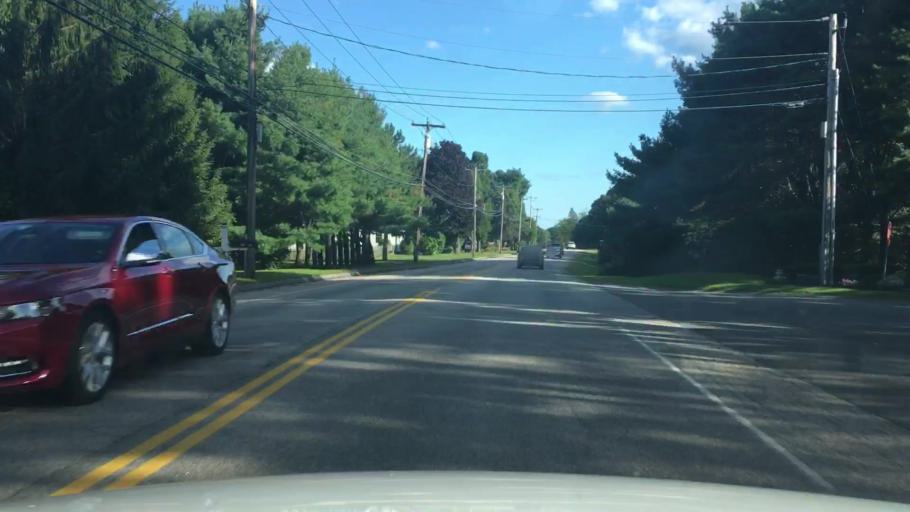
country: US
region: Maine
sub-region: Cumberland County
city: Scarborough
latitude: 43.5739
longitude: -70.3187
